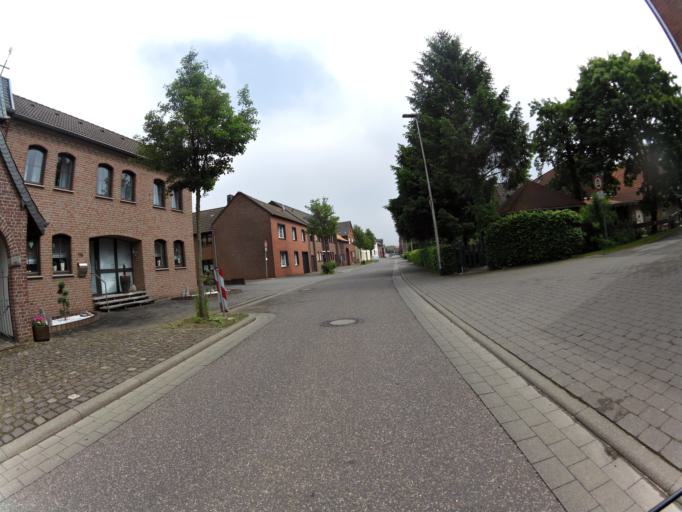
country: DE
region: North Rhine-Westphalia
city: Geilenkirchen
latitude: 50.9904
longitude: 6.0931
